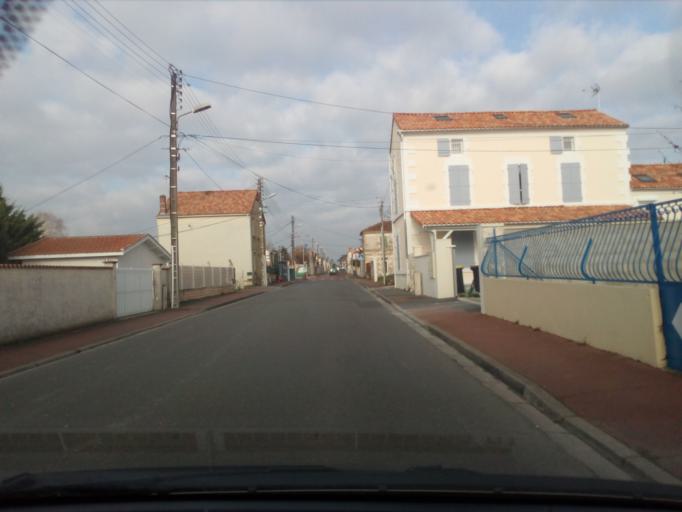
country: FR
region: Poitou-Charentes
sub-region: Departement de la Charente
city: Gond-Pontouvre
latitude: 45.6761
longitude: 0.1581
